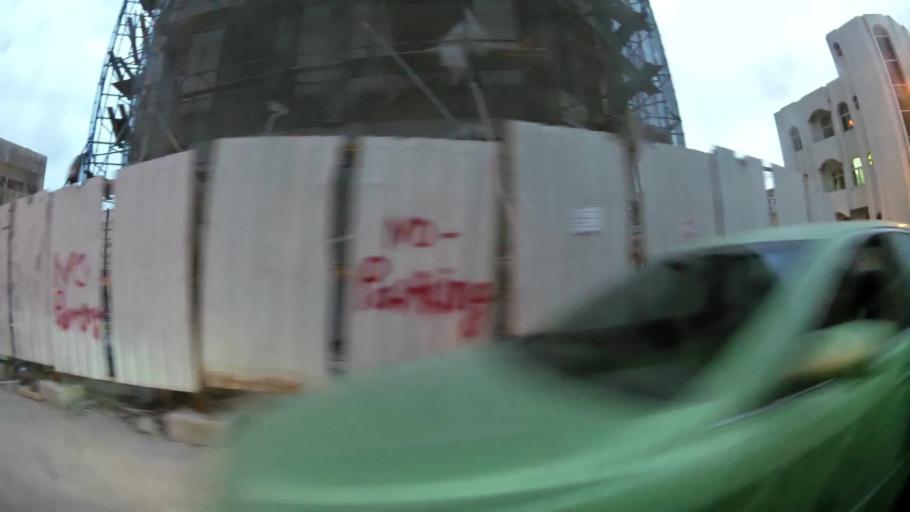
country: QA
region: Baladiyat ad Dawhah
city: Doha
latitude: 25.2692
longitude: 51.5256
